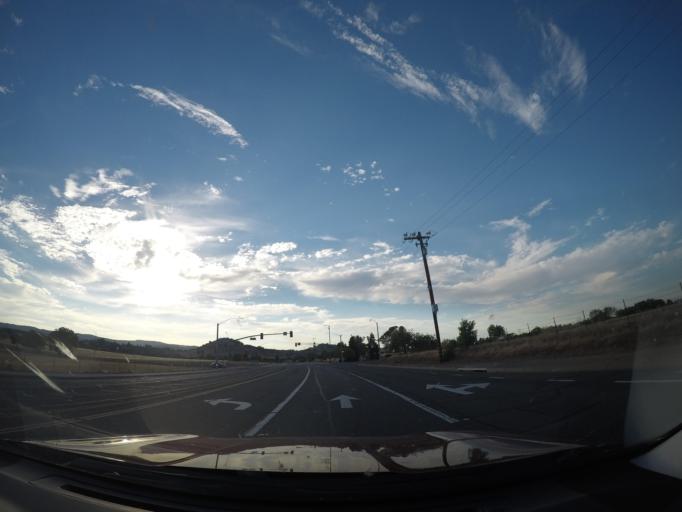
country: US
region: California
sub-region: Solano County
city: Vacaville
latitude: 38.3690
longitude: -121.9702
